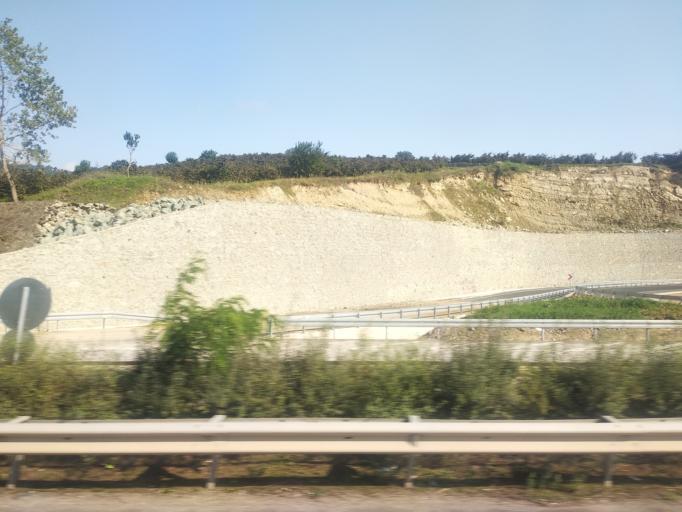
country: TR
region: Ordu
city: Ordu
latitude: 40.9940
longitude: 37.8171
